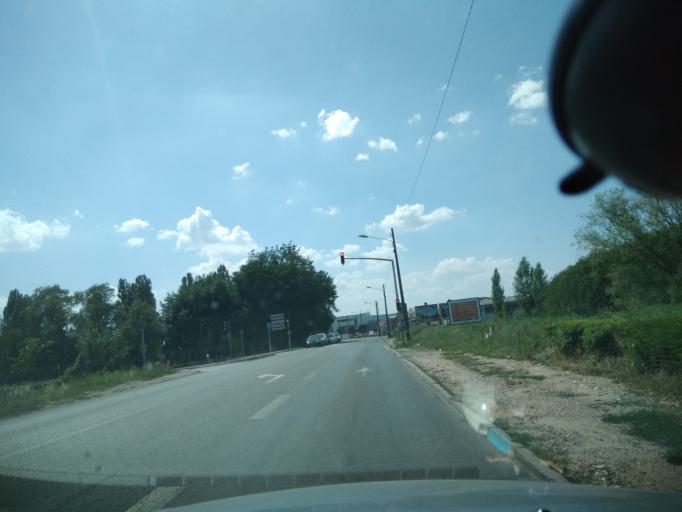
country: FR
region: Centre
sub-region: Departement d'Indre-et-Loire
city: Saint-Pierre-des-Corps
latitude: 47.3811
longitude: 0.7361
